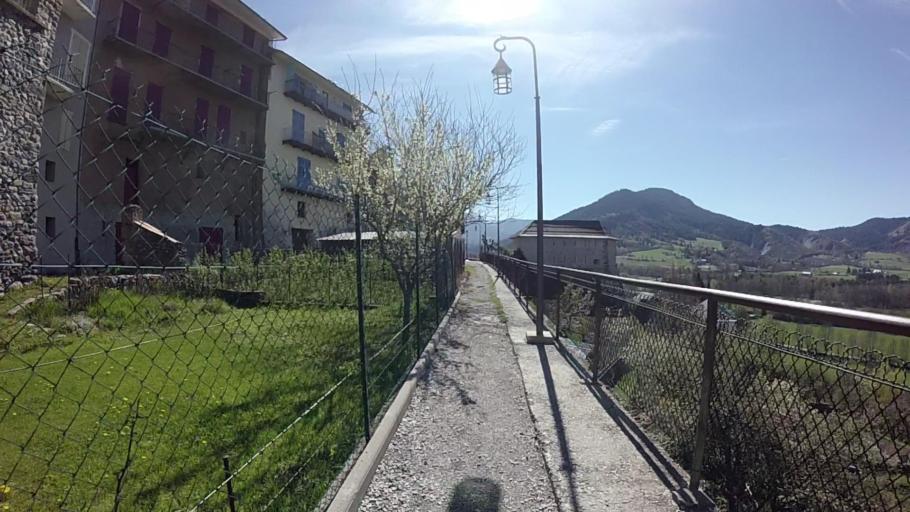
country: FR
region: Provence-Alpes-Cote d'Azur
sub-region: Departement des Alpes-de-Haute-Provence
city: Seyne-les-Alpes
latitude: 44.3501
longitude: 6.3549
